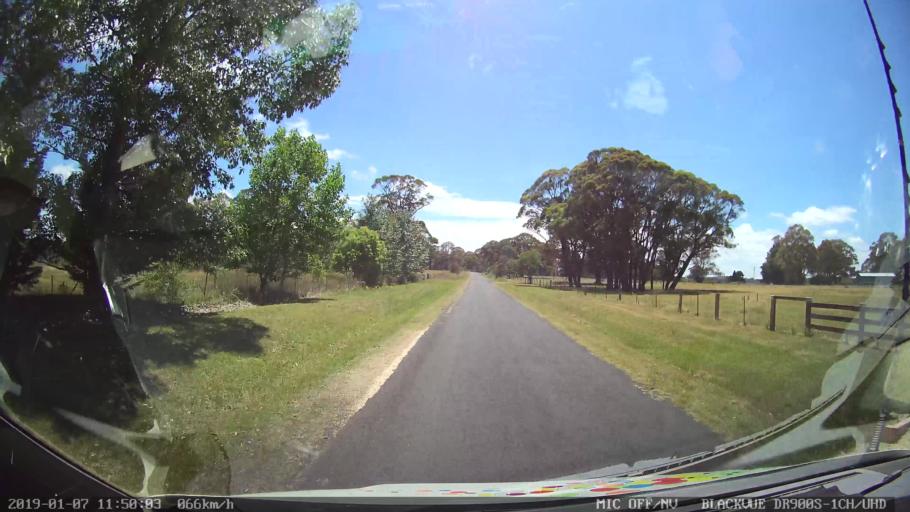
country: AU
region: New South Wales
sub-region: Guyra
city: Guyra
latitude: -30.3141
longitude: 151.6319
